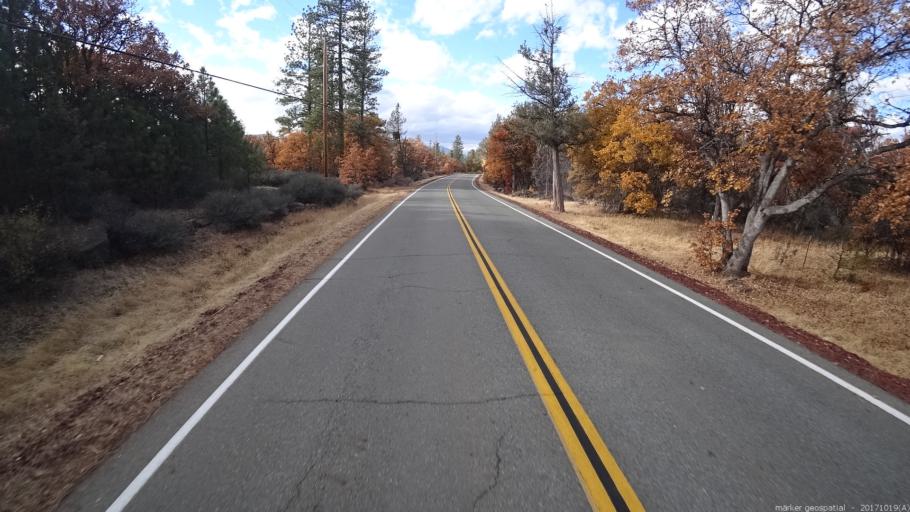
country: US
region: California
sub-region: Shasta County
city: Burney
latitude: 40.9951
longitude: -121.4318
